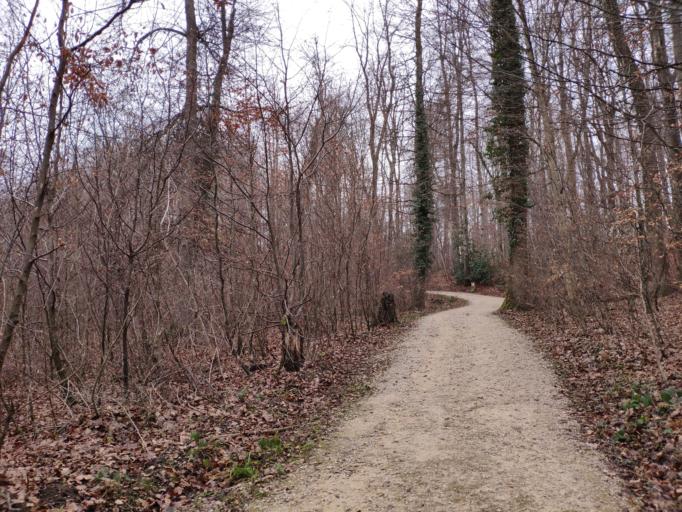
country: CH
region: Basel-City
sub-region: Basel-Stadt
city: Bettingen
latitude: 47.5624
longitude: 7.6556
